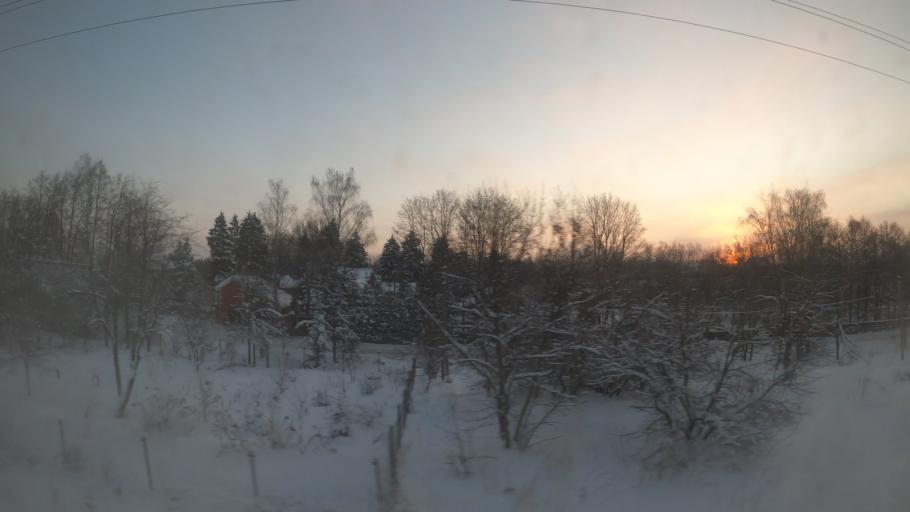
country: RU
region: Moskovskaya
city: Yermolino
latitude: 56.1303
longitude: 37.5203
